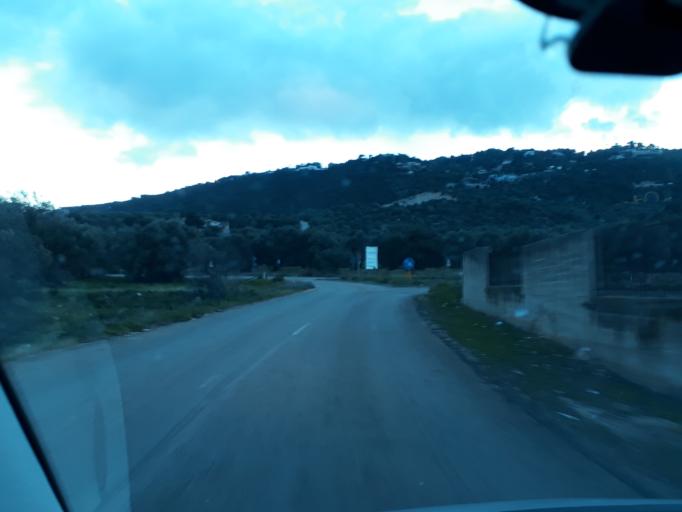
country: IT
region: Apulia
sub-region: Provincia di Brindisi
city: Fasano
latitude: 40.8330
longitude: 17.3510
